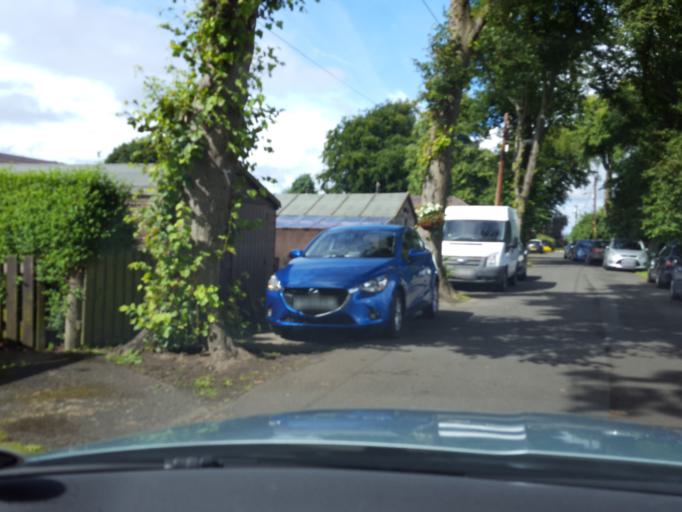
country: GB
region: Scotland
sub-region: West Lothian
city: Linlithgow
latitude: 56.0071
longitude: -3.5730
